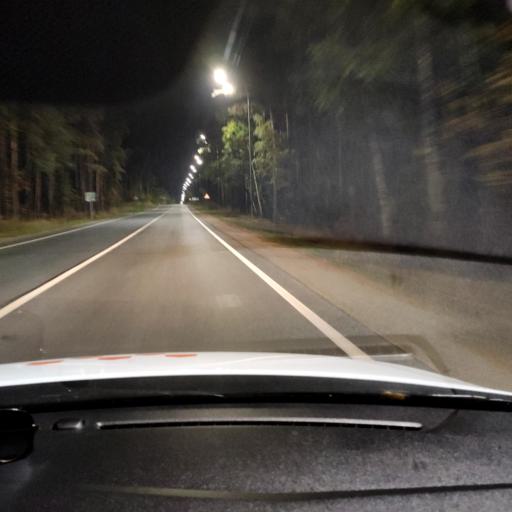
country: RU
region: Tatarstan
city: Verkhniy Uslon
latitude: 55.6398
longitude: 49.0260
